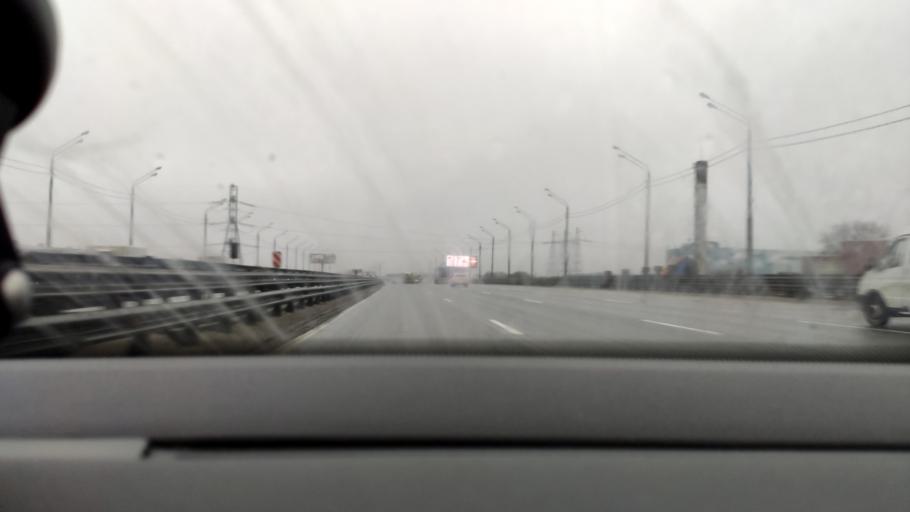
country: RU
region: Moskovskaya
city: Arkhangel'skoye
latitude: 55.8036
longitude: 37.3081
